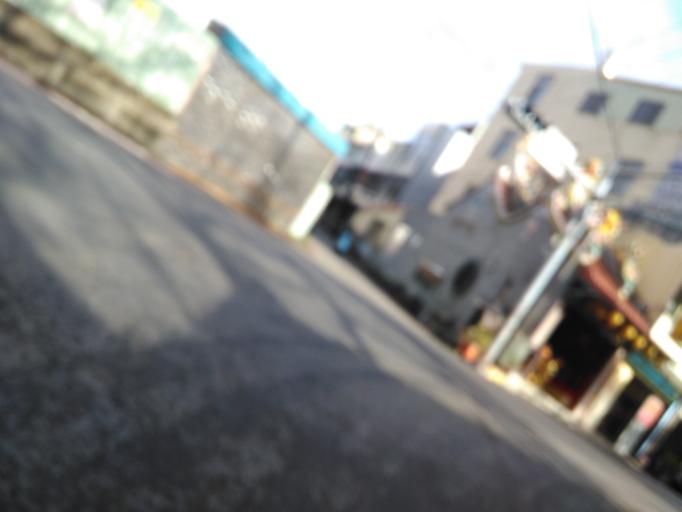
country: TW
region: Taiwan
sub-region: Hsinchu
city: Zhubei
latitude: 24.7858
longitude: 121.0215
